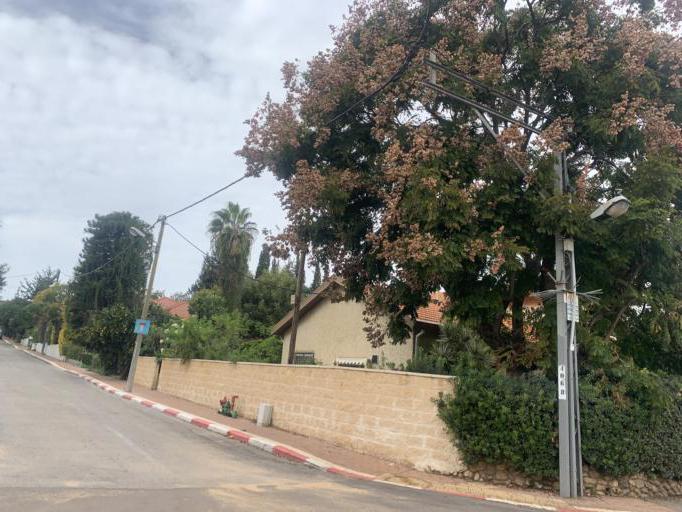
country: IL
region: Central District
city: Hod HaSharon
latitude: 32.1665
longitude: 34.8836
